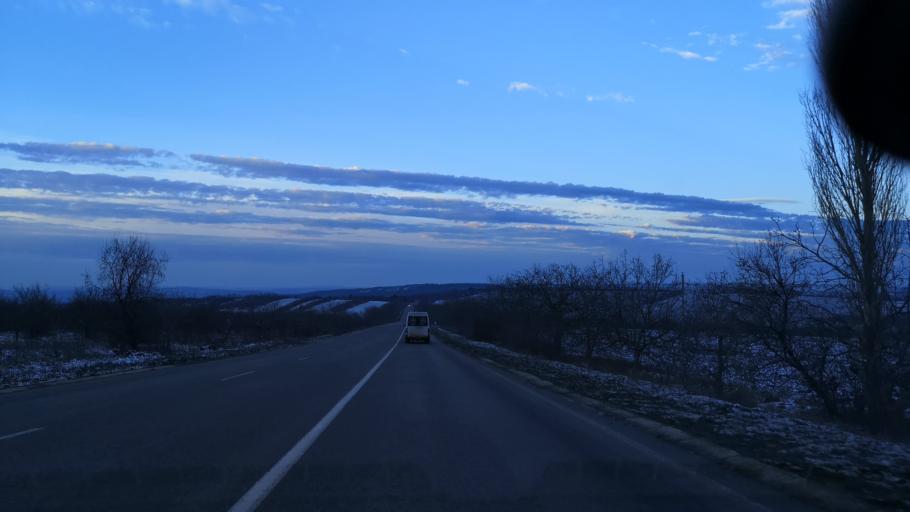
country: MD
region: Orhei
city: Orhei
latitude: 47.5383
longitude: 28.7932
